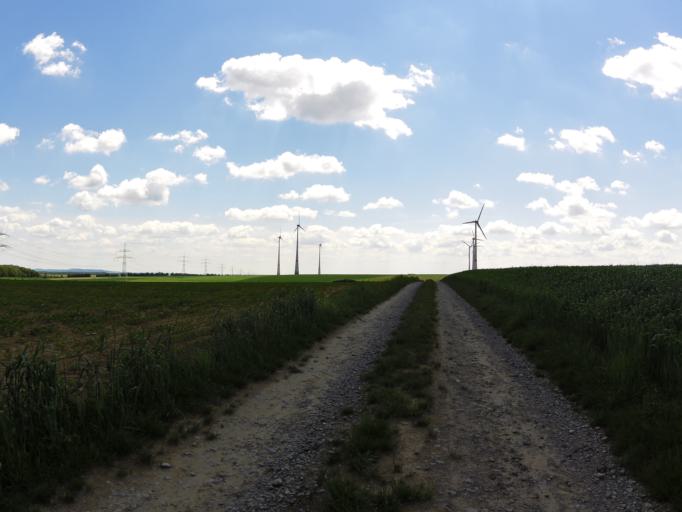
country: DE
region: Bavaria
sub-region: Regierungsbezirk Unterfranken
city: Theilheim
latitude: 49.7307
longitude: 10.0419
